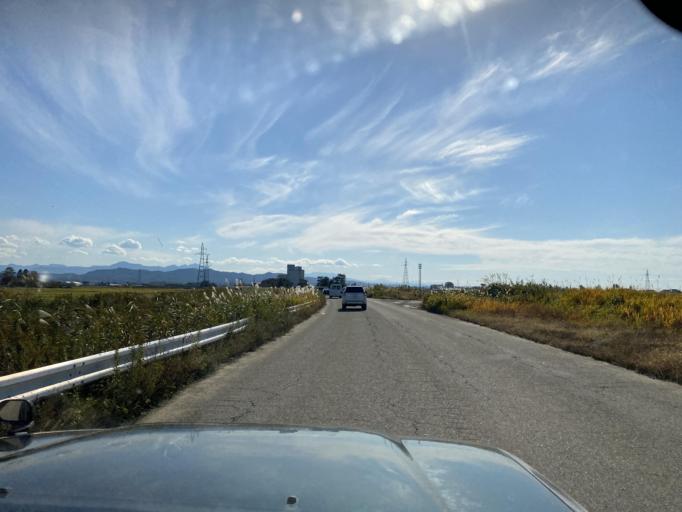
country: JP
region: Niigata
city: Niitsu-honcho
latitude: 37.8002
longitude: 139.0768
